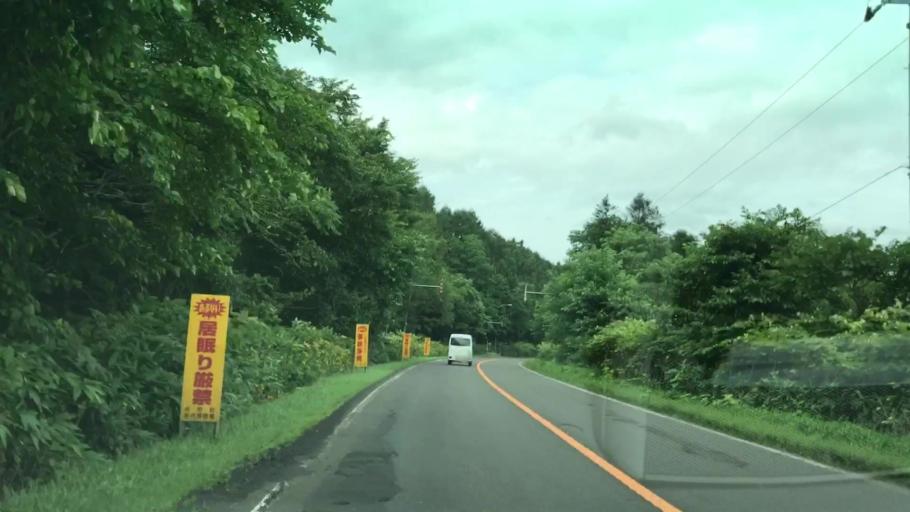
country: JP
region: Hokkaido
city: Niseko Town
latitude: 42.9508
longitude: 140.6992
